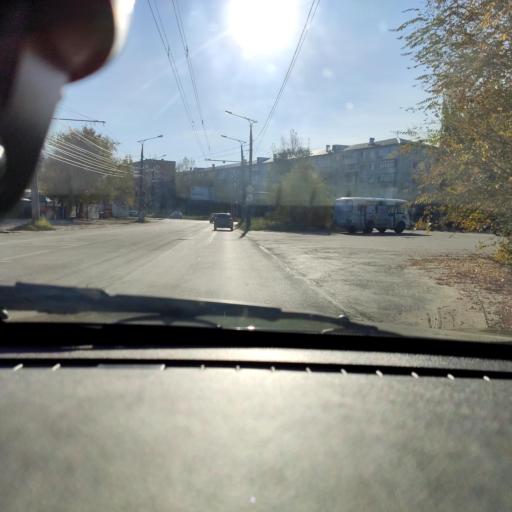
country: RU
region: Samara
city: Tol'yatti
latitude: 53.5153
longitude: 49.4296
